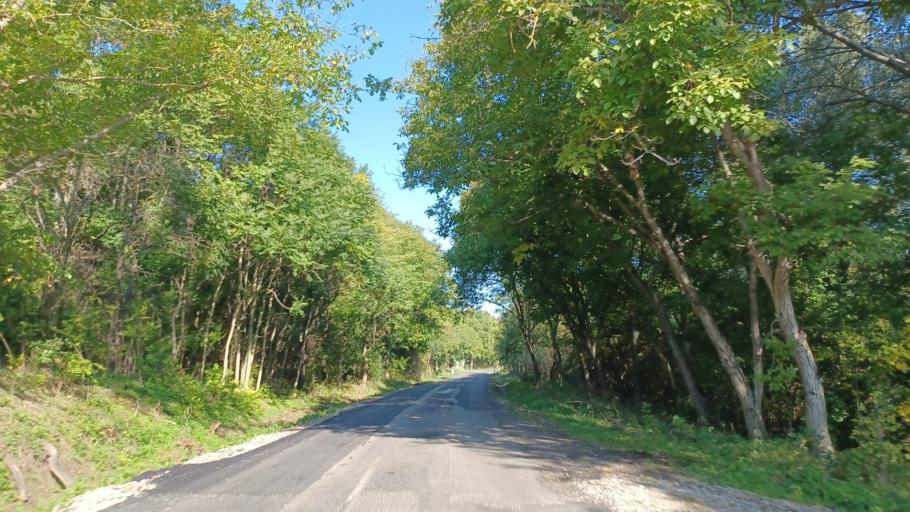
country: HU
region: Tolna
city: Nagydorog
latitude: 46.5733
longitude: 18.5905
